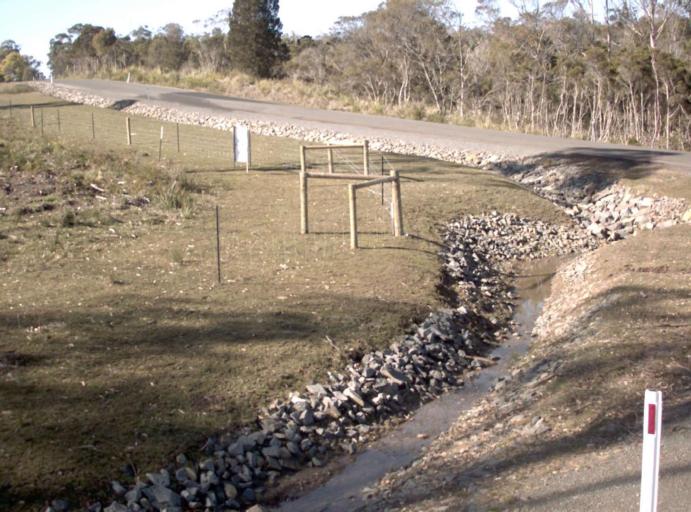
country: AU
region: Tasmania
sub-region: Launceston
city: Mayfield
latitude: -41.2820
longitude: 147.0290
